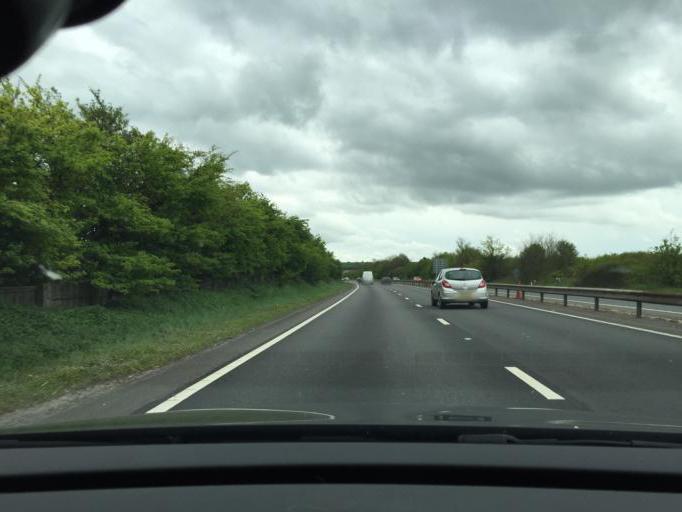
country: GB
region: England
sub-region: Oxfordshire
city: Harwell
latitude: 51.5669
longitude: -1.3011
